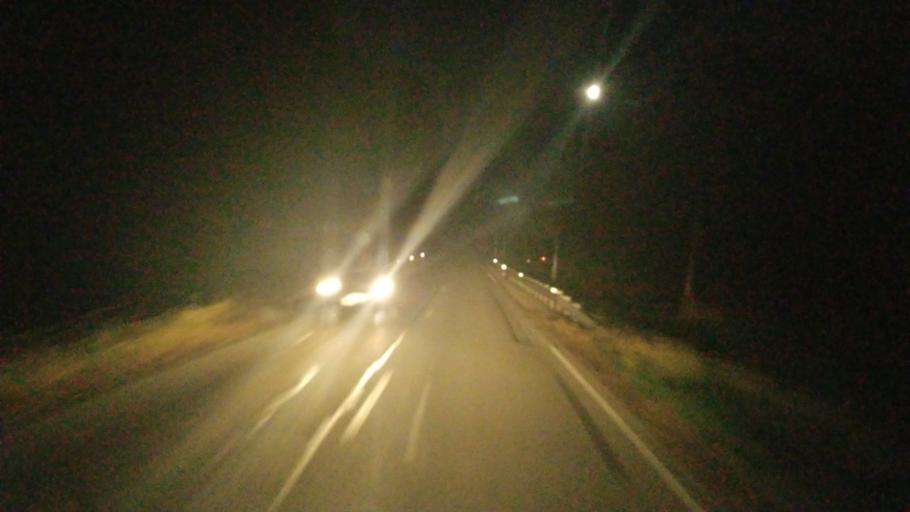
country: US
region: Ohio
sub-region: Union County
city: Richwood
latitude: 40.5711
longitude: -83.2970
